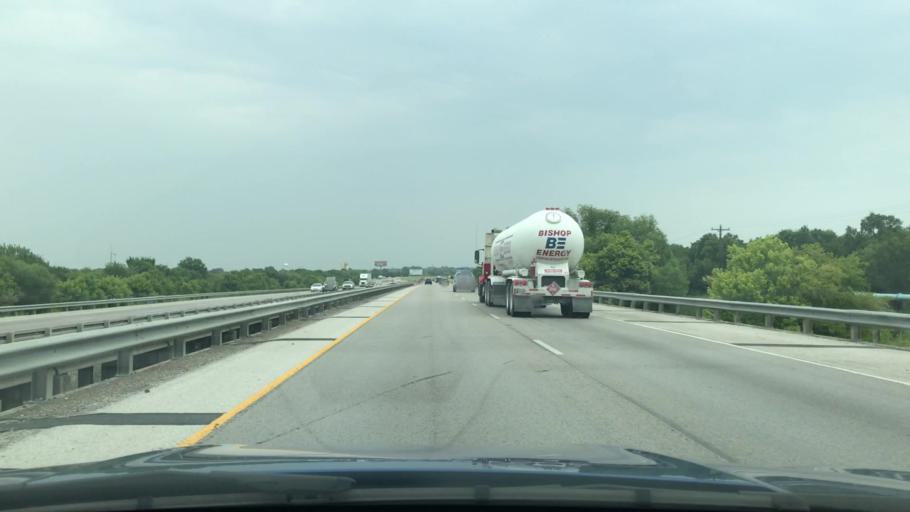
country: US
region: Texas
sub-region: Kaufman County
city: Forney
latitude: 32.7741
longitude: -96.5022
